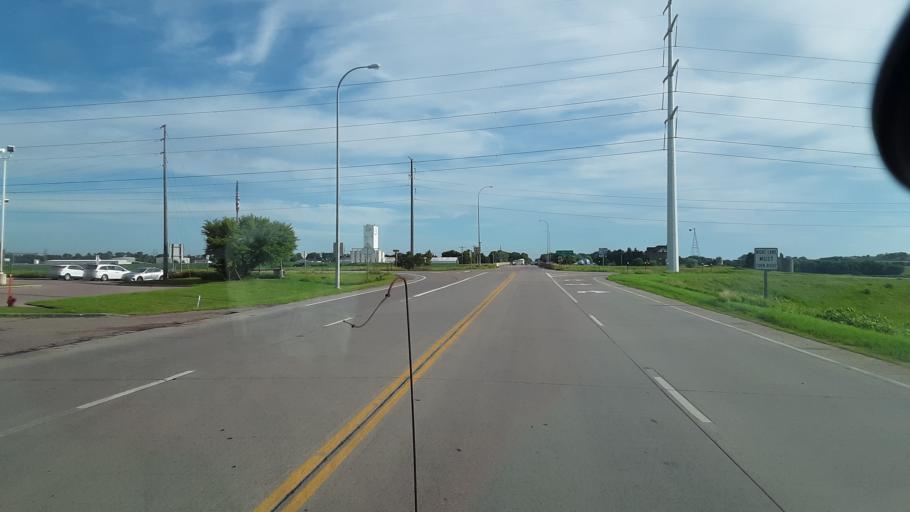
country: US
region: South Dakota
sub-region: Minnehaha County
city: Brandon
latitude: 43.6068
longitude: -96.5722
